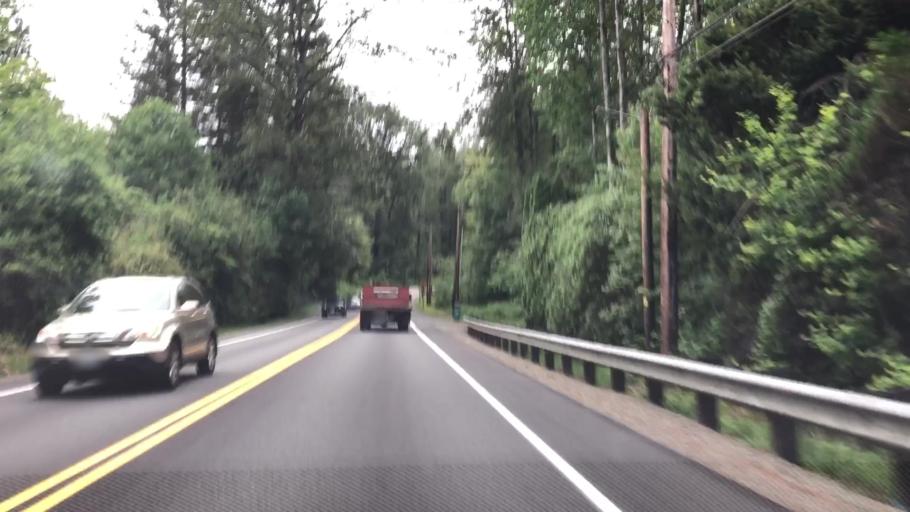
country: US
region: Washington
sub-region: King County
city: Cottage Lake
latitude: 47.7549
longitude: -122.0578
